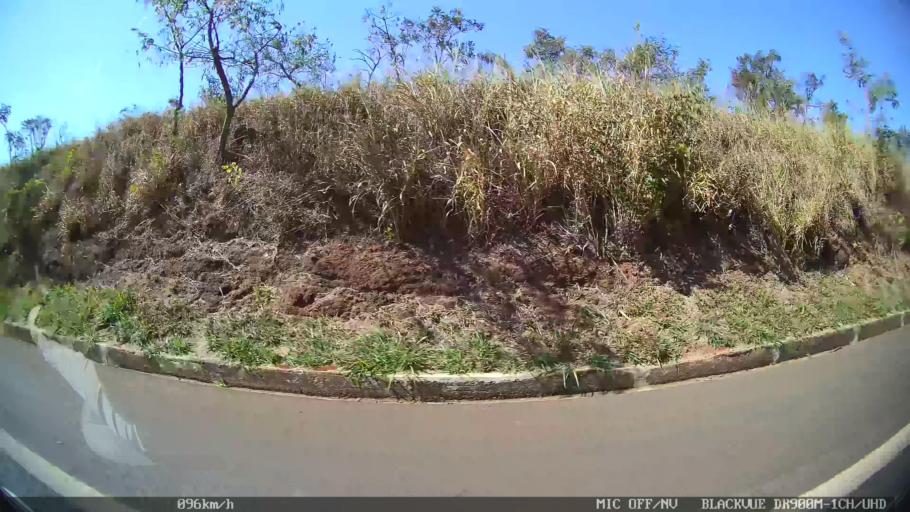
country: BR
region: Sao Paulo
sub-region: Batatais
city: Batatais
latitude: -20.7380
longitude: -47.5305
